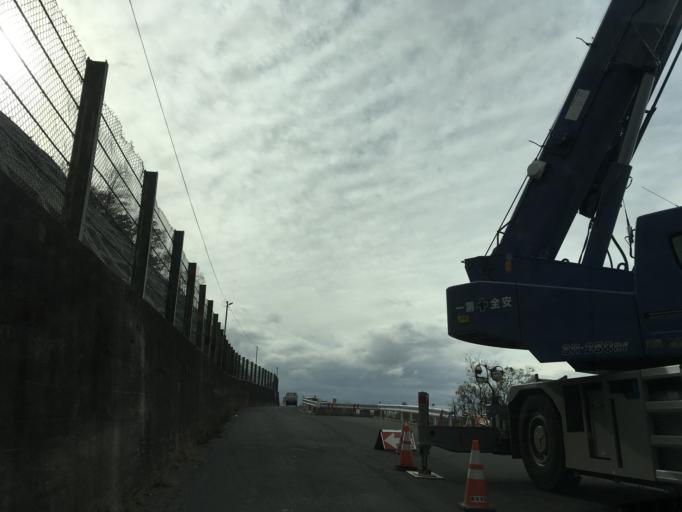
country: JP
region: Iwate
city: Ichinoseki
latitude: 38.7494
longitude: 141.2840
